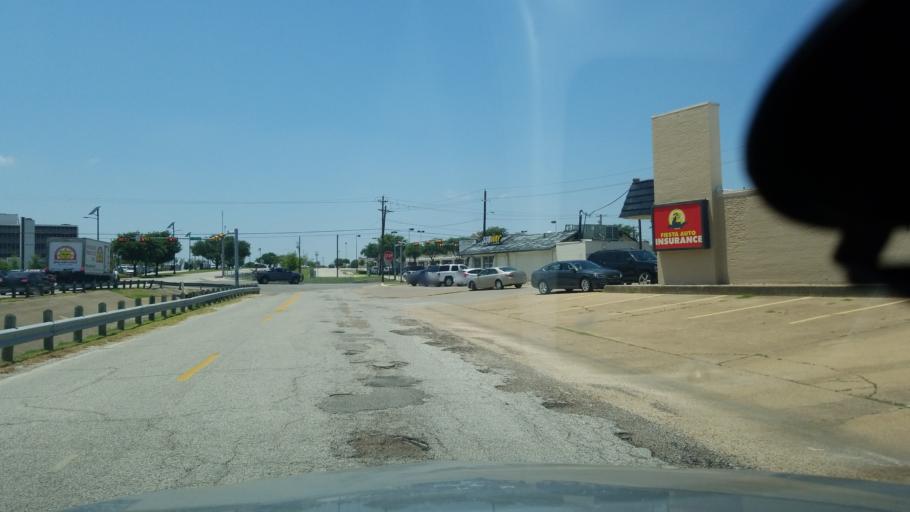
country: US
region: Texas
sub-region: Dallas County
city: Irving
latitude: 32.8284
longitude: -96.9755
